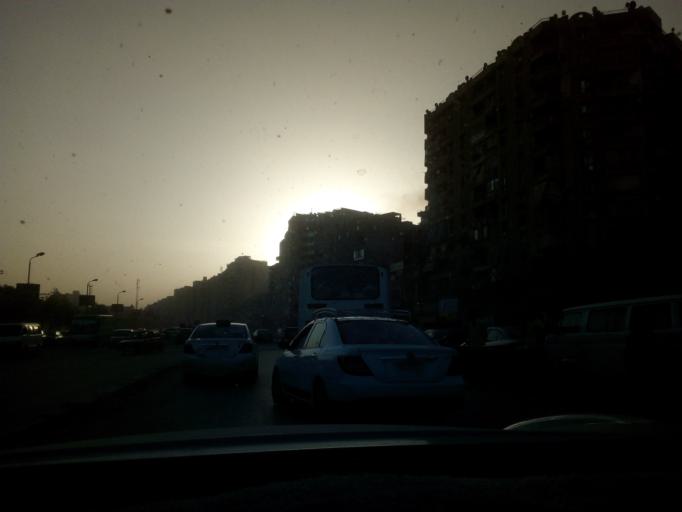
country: EG
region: Muhafazat al Qalyubiyah
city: Al Khankah
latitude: 30.1241
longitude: 31.3468
